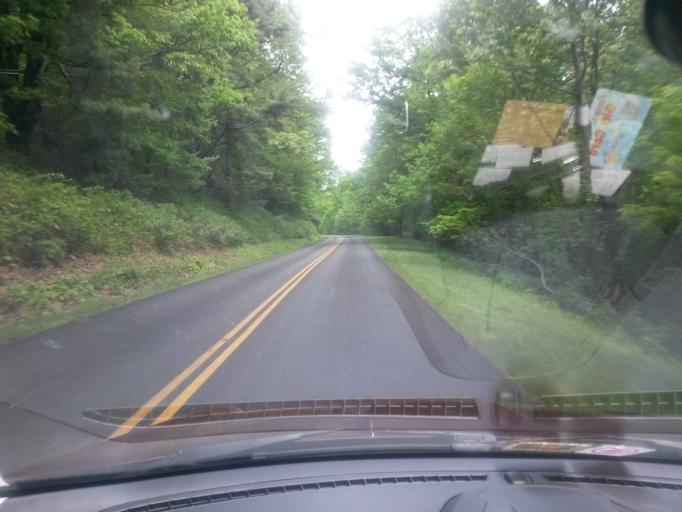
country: US
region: Virginia
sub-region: Floyd County
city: Floyd
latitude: 36.8323
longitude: -80.3418
